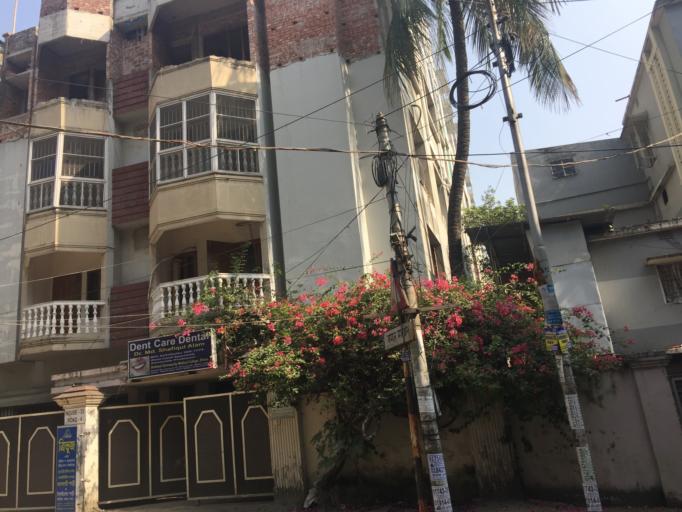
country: BD
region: Dhaka
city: Azimpur
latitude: 23.7402
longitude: 90.3783
